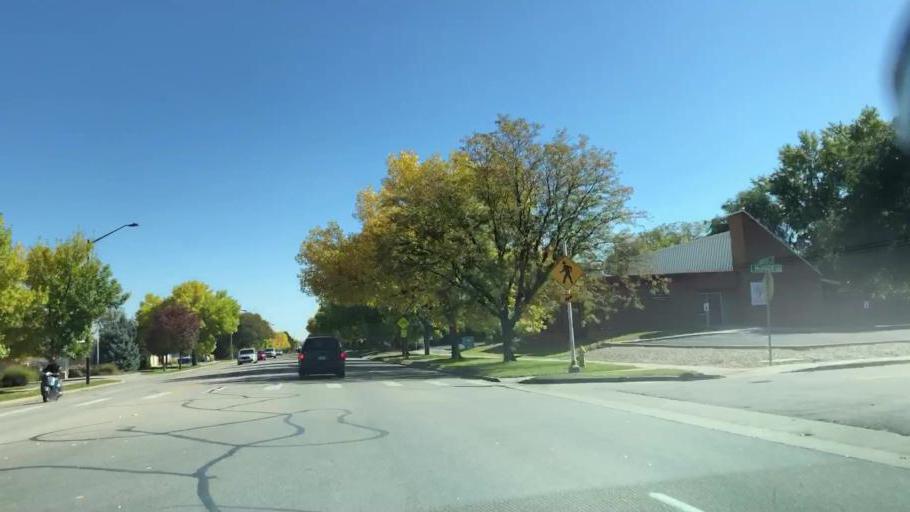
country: US
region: Colorado
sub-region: Larimer County
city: Fort Collins
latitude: 40.5749
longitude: -105.0535
